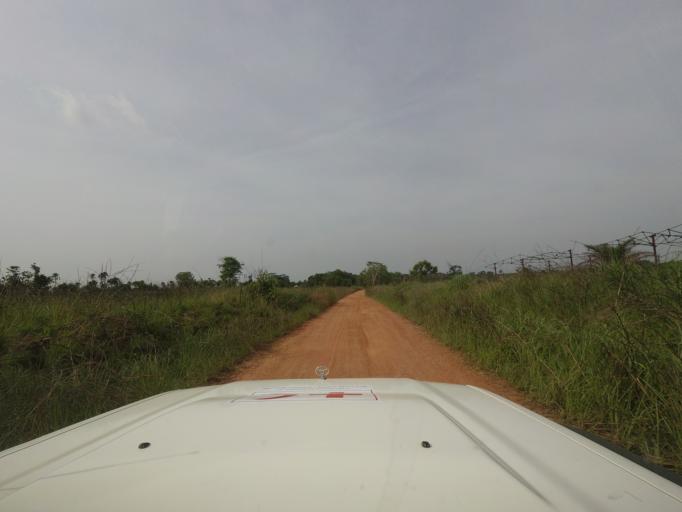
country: GN
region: Nzerekore
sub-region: Macenta
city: Macenta
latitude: 8.5347
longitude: -9.5016
